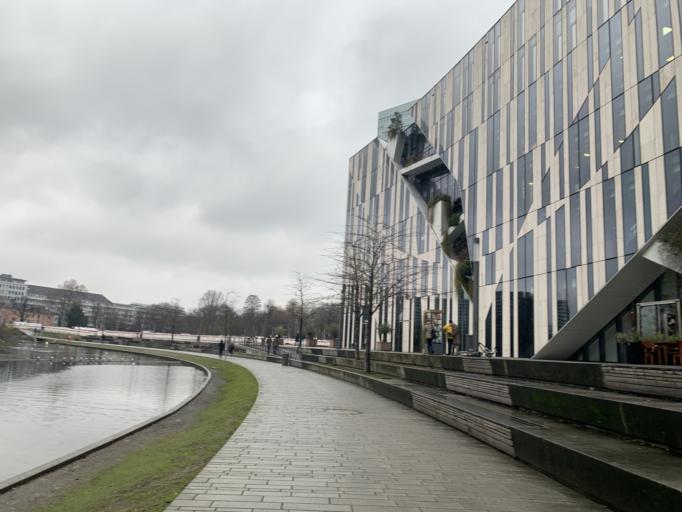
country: DE
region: North Rhine-Westphalia
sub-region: Regierungsbezirk Dusseldorf
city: Dusseldorf
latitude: 51.2273
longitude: 6.7801
